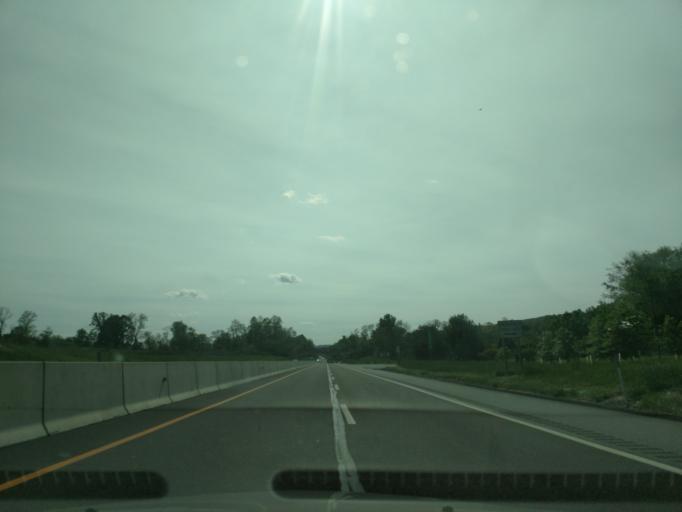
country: US
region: Pennsylvania
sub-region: Lancaster County
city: Clay
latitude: 40.2445
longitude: -76.2296
